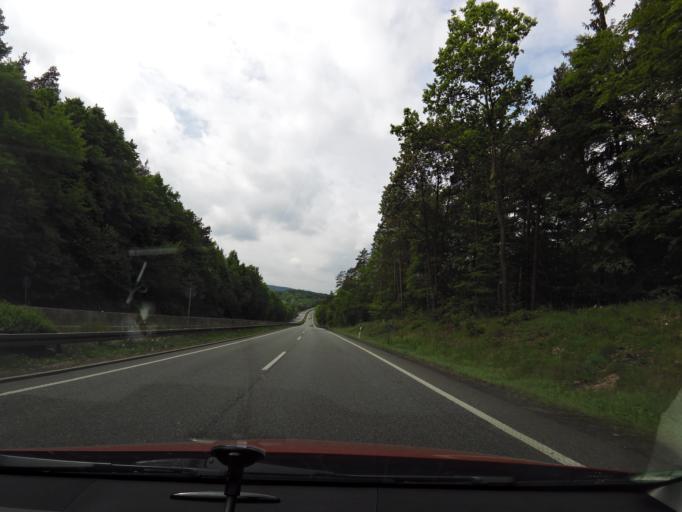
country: DE
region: Thuringia
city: Grossensee
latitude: 50.9513
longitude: 9.9730
